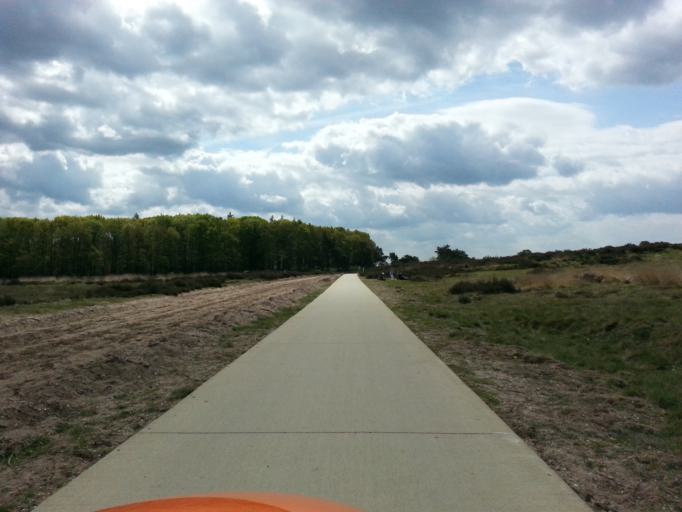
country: NL
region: Gelderland
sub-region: Gemeente Ede
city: Ede
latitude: 52.0531
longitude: 5.7052
